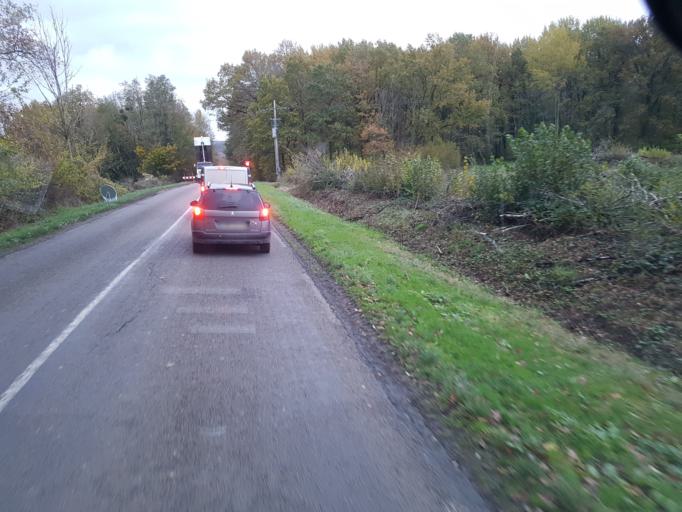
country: FR
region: Picardie
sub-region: Departement de l'Aisne
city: Nesles-la-Montagne
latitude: 49.0102
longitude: 3.4200
